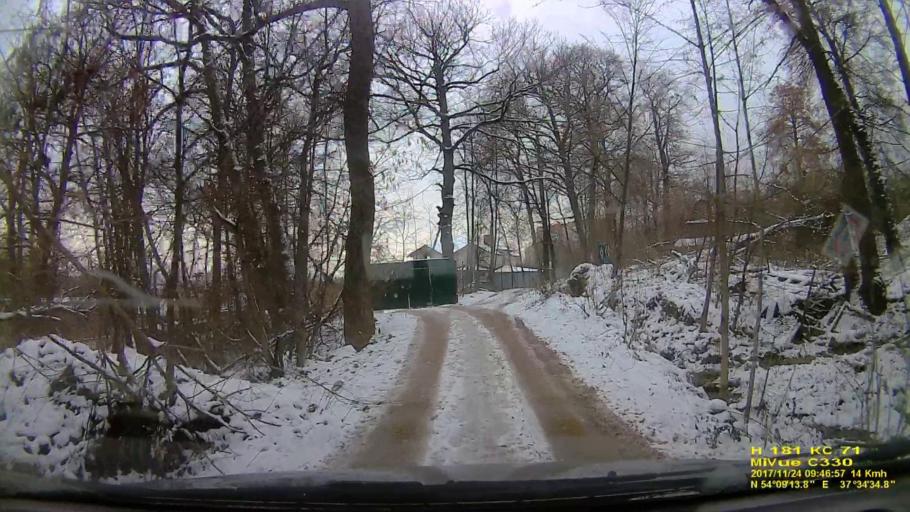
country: RU
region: Tula
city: Mendeleyevskiy
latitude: 54.1539
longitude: 37.5762
